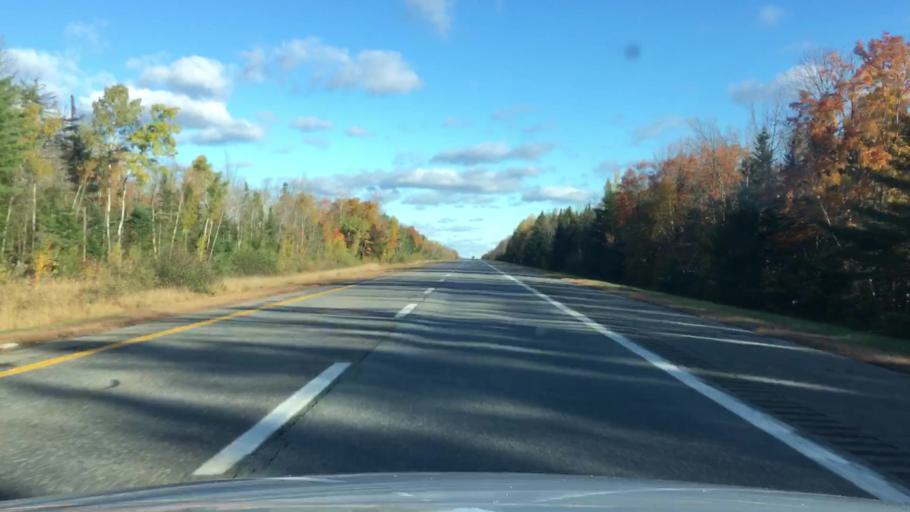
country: US
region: Maine
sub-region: Penobscot County
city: Greenbush
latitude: 45.0748
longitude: -68.6911
